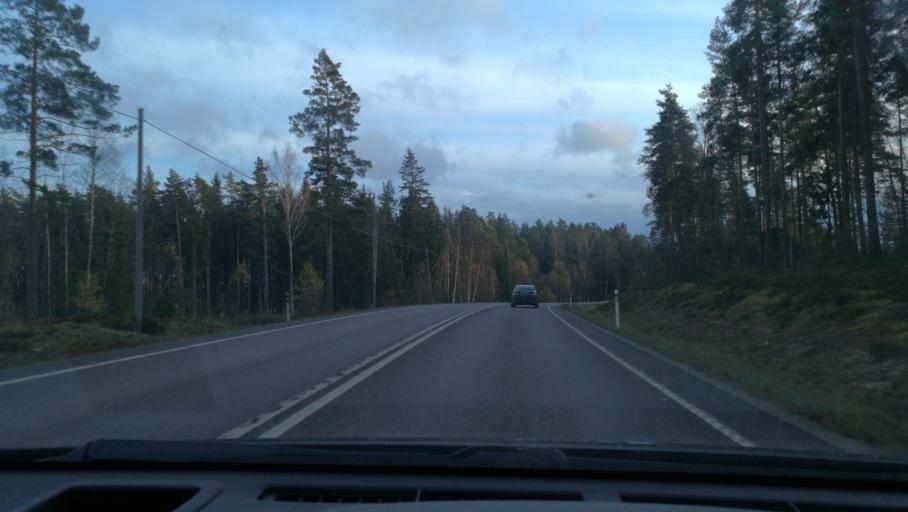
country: SE
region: Soedermanland
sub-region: Katrineholms Kommun
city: Katrineholm
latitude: 59.1766
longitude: 16.1151
